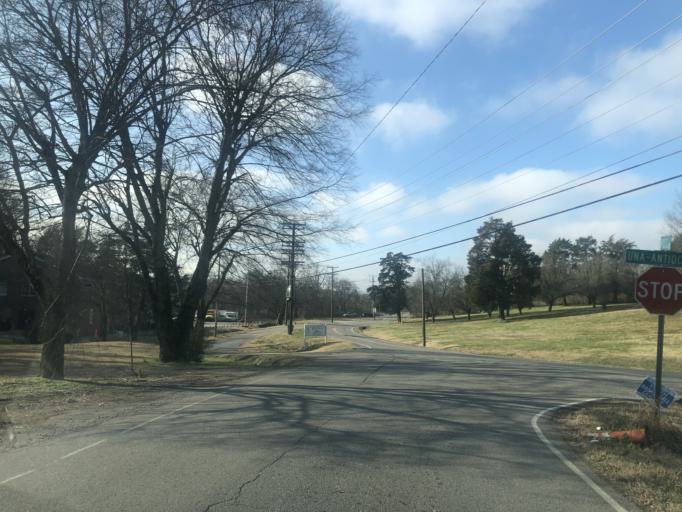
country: US
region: Tennessee
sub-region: Rutherford County
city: La Vergne
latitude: 36.0594
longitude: -86.6684
